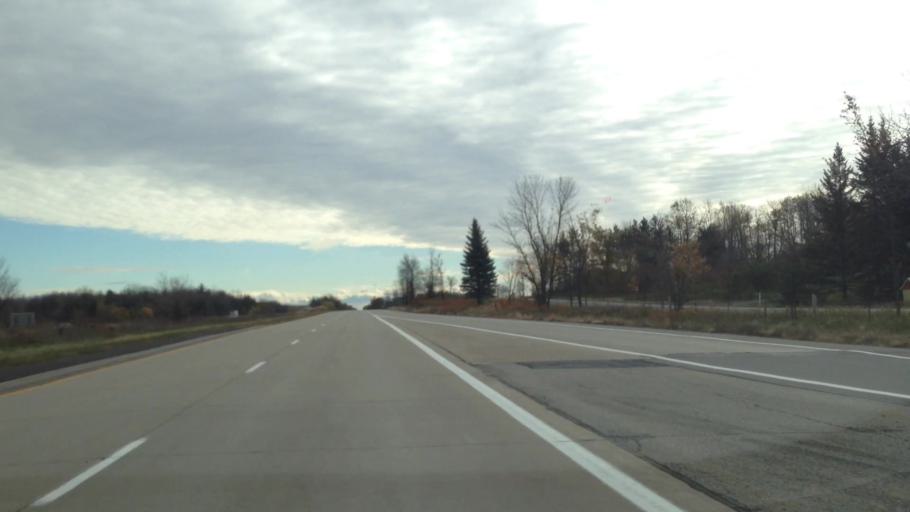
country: CA
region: Ontario
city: Hawkesbury
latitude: 45.5647
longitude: -74.4974
